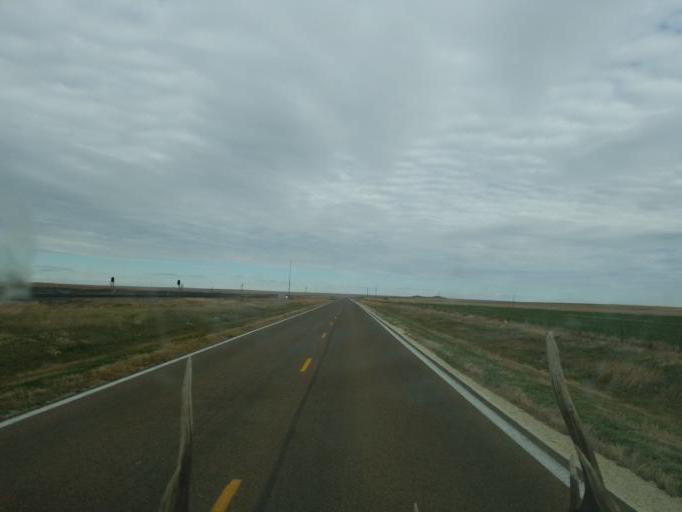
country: US
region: Kansas
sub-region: Wallace County
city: Sharon Springs
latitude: 38.9927
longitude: -101.4097
